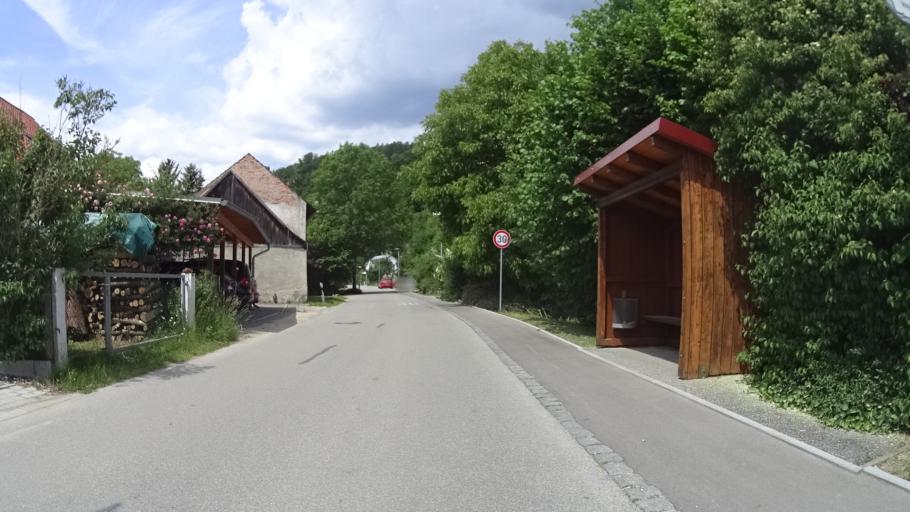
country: DE
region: Bavaria
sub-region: Lower Bavaria
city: Bad Abbach
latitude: 48.9511
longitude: 12.0114
